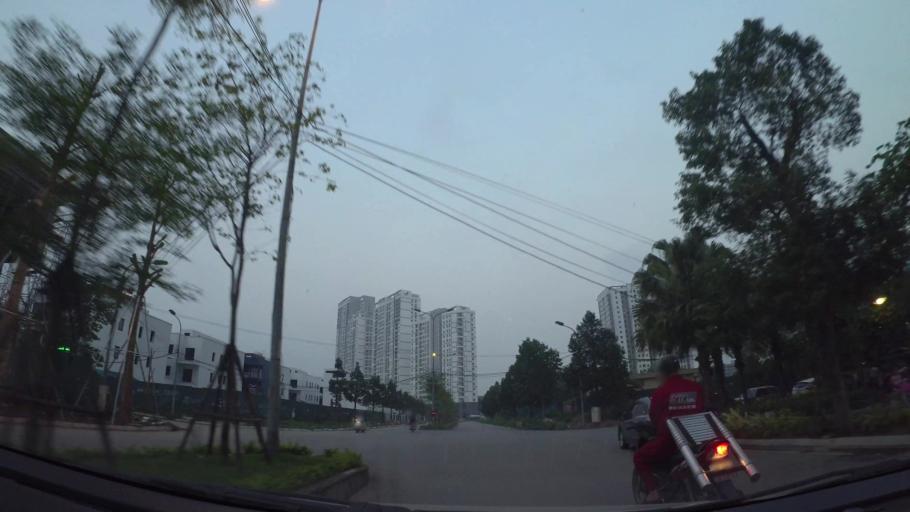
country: VN
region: Ha Noi
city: Tay Ho
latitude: 21.0674
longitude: 105.7986
